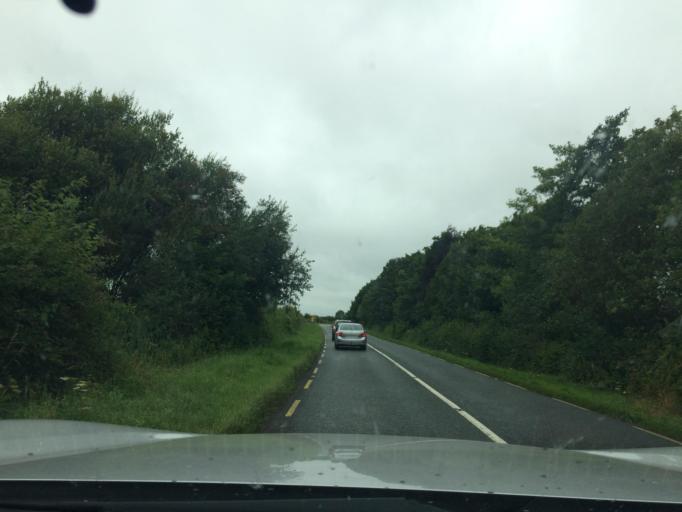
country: IE
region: Munster
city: Cashel
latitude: 52.4753
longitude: -7.8473
